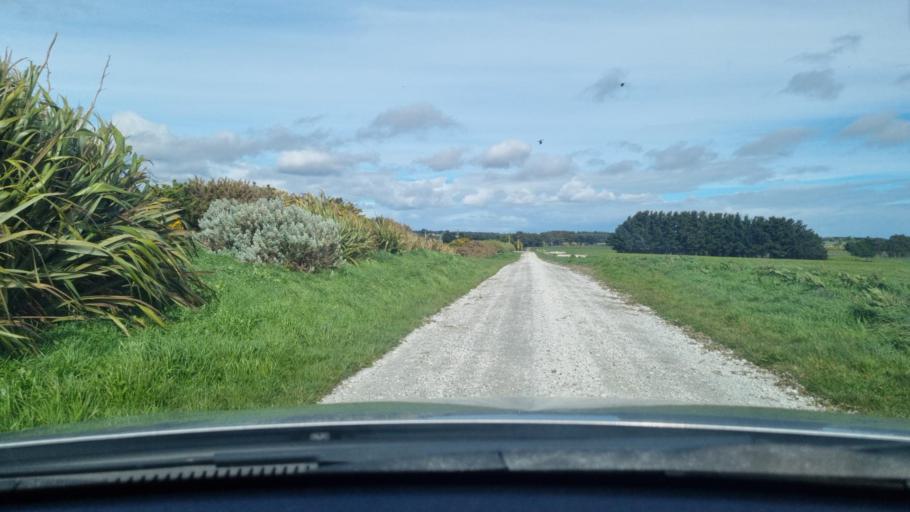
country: NZ
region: Southland
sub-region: Invercargill City
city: Invercargill
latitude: -46.4562
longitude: 168.3860
